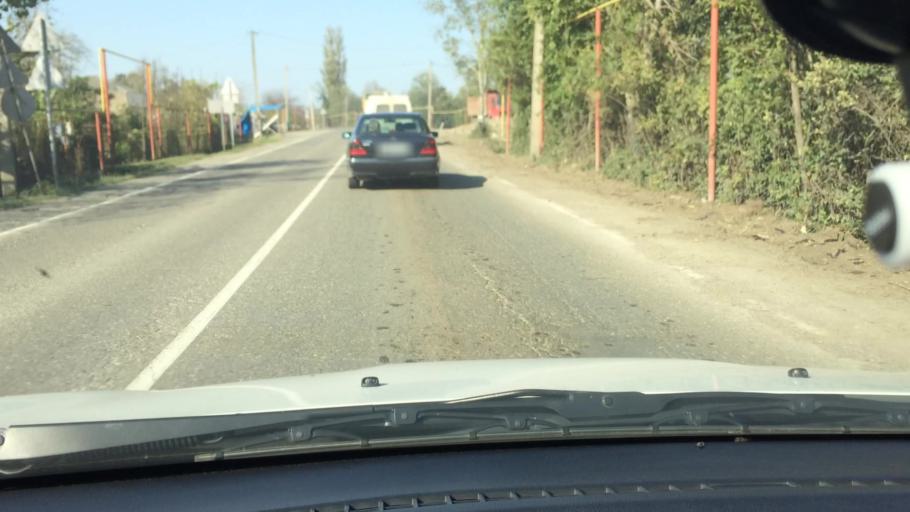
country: GE
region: Guria
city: Lanchkhuti
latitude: 42.0750
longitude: 42.0757
